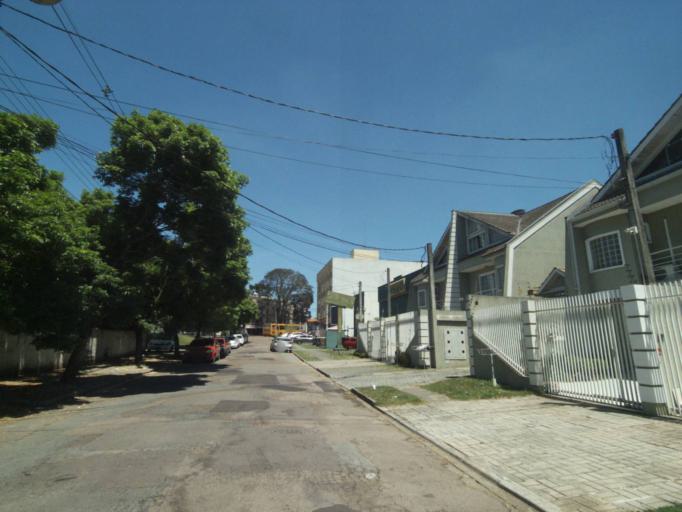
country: BR
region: Parana
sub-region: Curitiba
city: Curitiba
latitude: -25.3933
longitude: -49.2288
